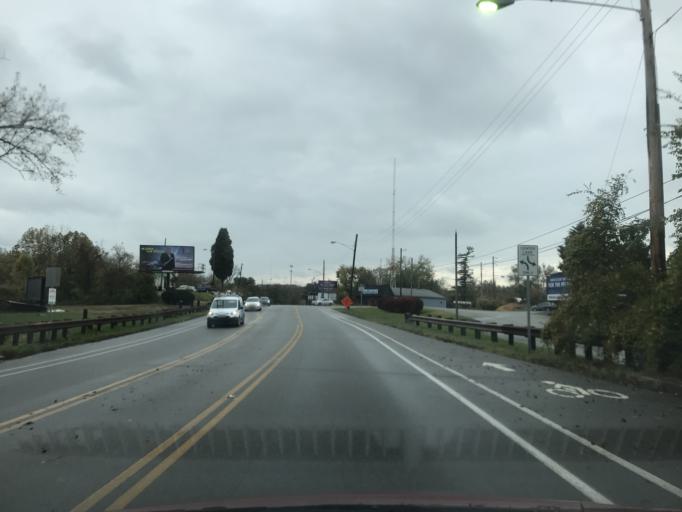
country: US
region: Indiana
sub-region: Clark County
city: Jeffersonville
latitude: 38.2505
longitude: -85.7167
